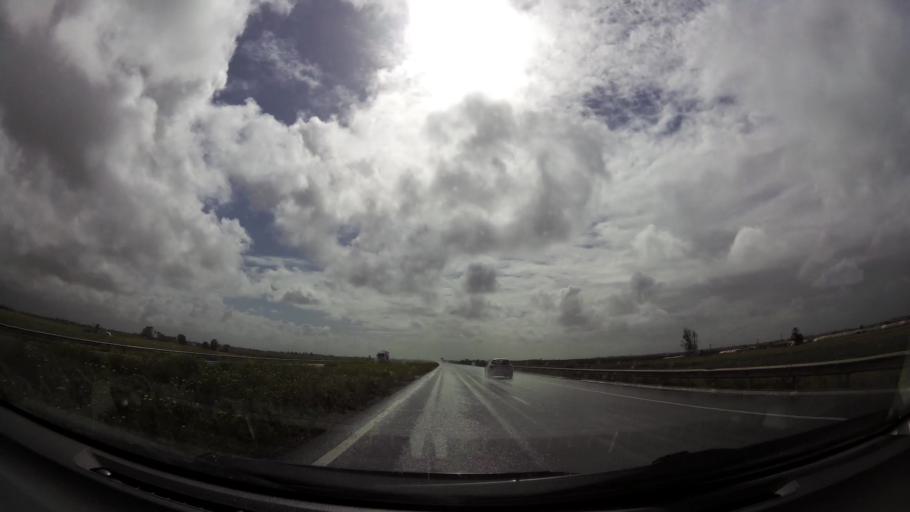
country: MA
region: Grand Casablanca
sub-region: Nouaceur
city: Dar Bouazza
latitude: 33.3648
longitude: -7.9325
